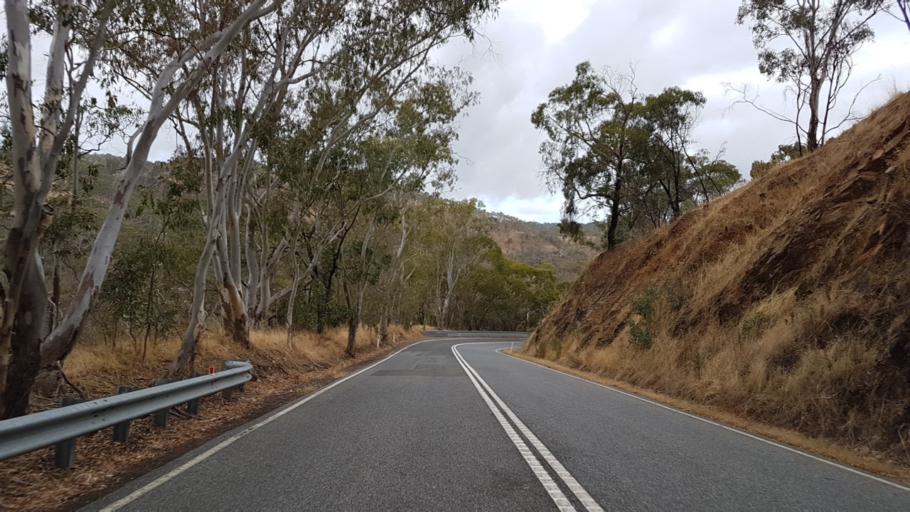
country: AU
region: South Australia
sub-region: Campbelltown
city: Athelstone
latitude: -34.8584
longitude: 138.7869
